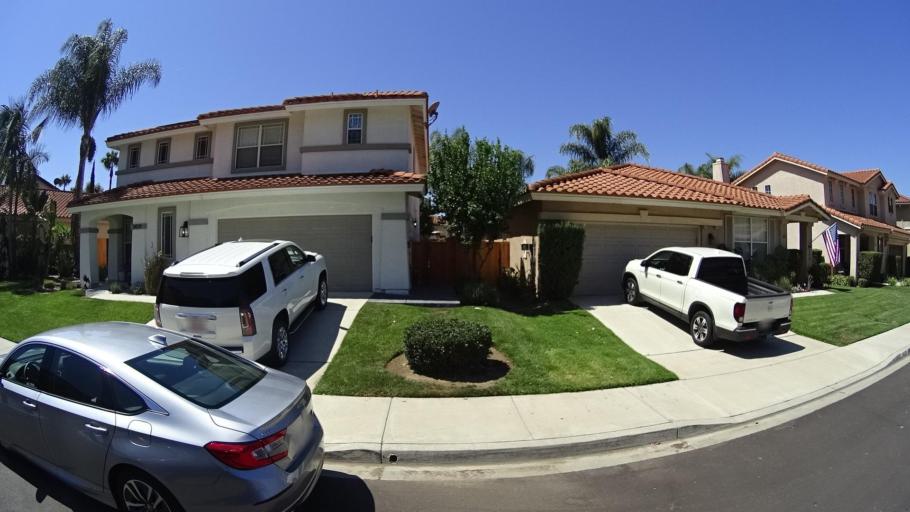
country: US
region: California
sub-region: San Diego County
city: Rainbow
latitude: 33.3263
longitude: -117.1490
